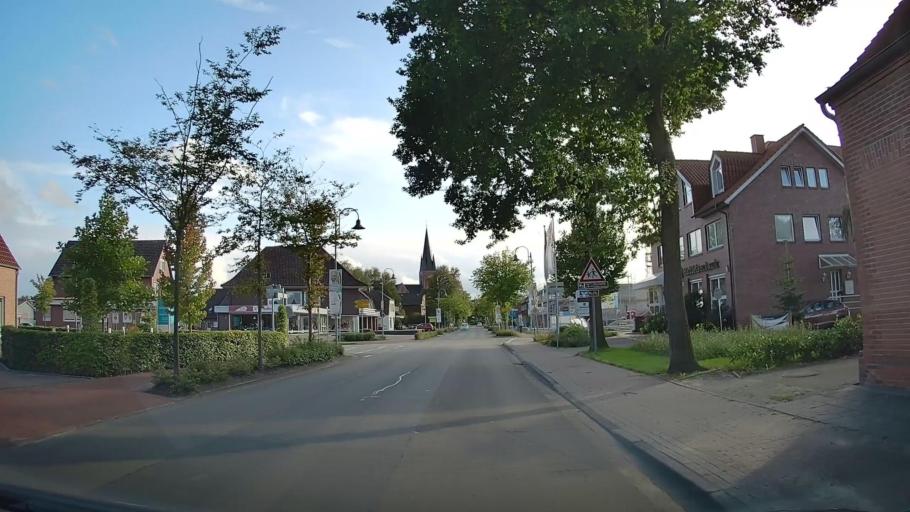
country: DE
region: Lower Saxony
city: Ostrhauderfehn
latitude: 53.1278
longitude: 7.6674
